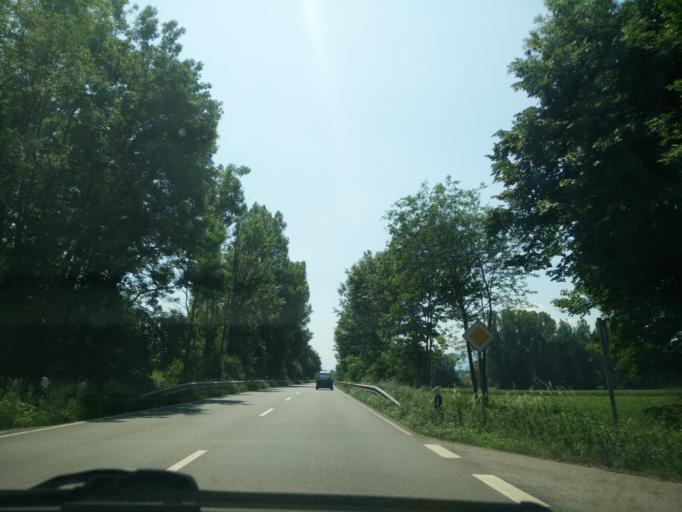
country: DE
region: Bavaria
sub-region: Upper Bavaria
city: Freilassing
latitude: 47.8864
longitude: 12.9658
